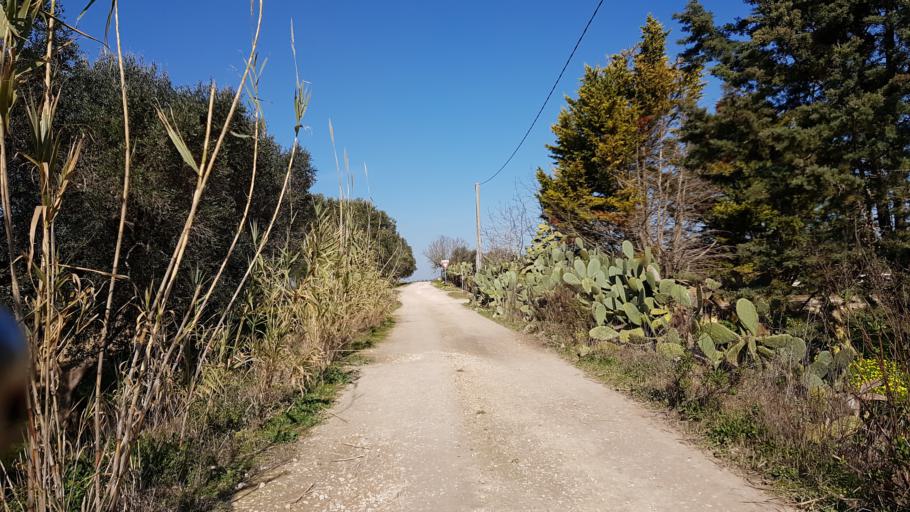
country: IT
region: Apulia
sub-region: Provincia di Brindisi
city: Mesagne
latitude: 40.6200
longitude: 17.8010
